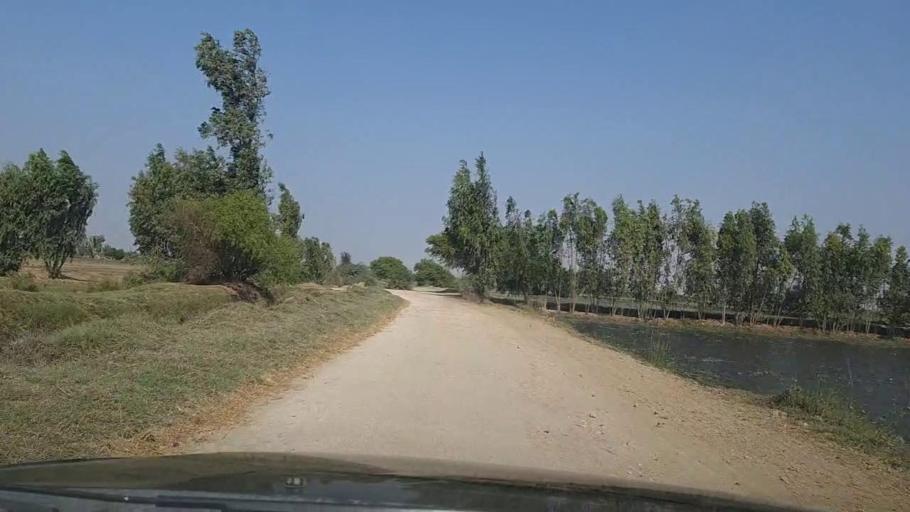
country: PK
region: Sindh
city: Thatta
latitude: 24.6249
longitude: 67.8140
